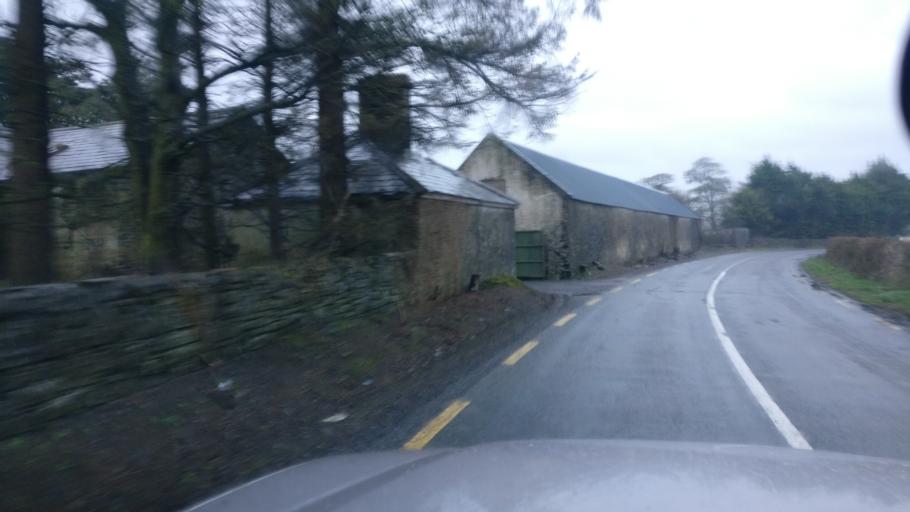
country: IE
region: Connaught
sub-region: County Galway
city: Ballinasloe
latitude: 53.2537
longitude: -8.1780
